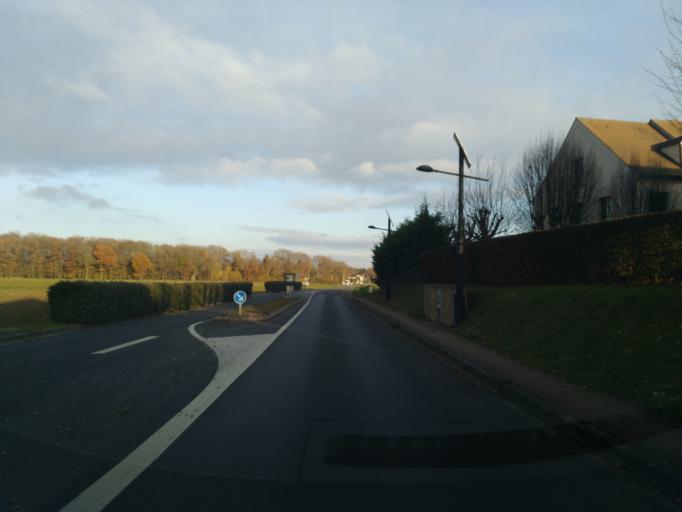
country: FR
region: Ile-de-France
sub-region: Departement des Yvelines
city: Neauphle-le-Chateau
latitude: 48.8159
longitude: 1.9094
